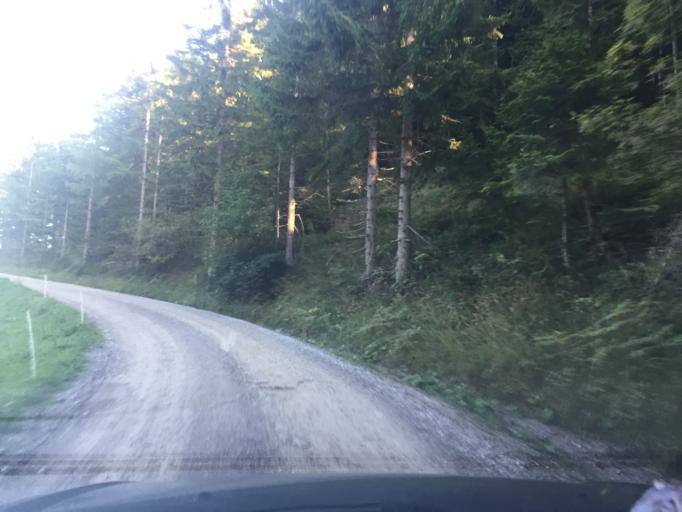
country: SI
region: Ravne na Koroskem
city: Kotlje
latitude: 46.4681
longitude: 14.9874
